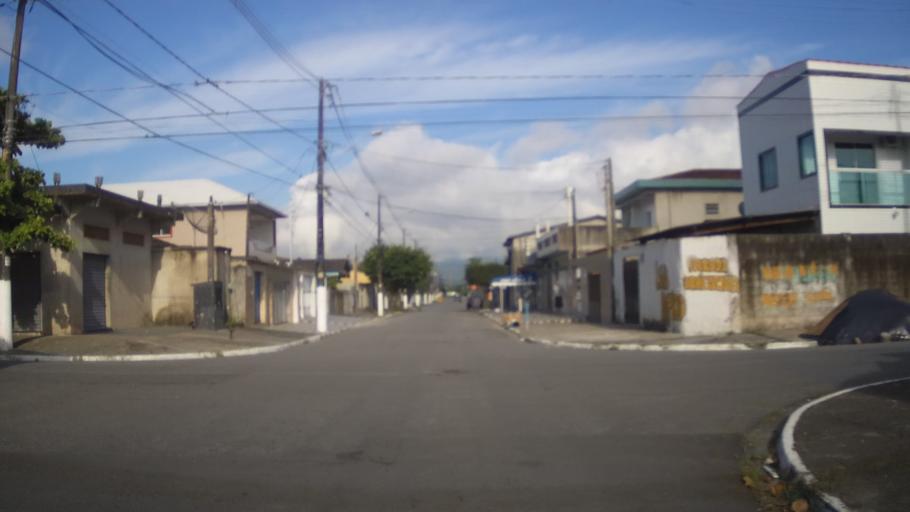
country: BR
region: Sao Paulo
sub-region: Praia Grande
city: Praia Grande
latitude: -24.0136
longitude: -46.4795
